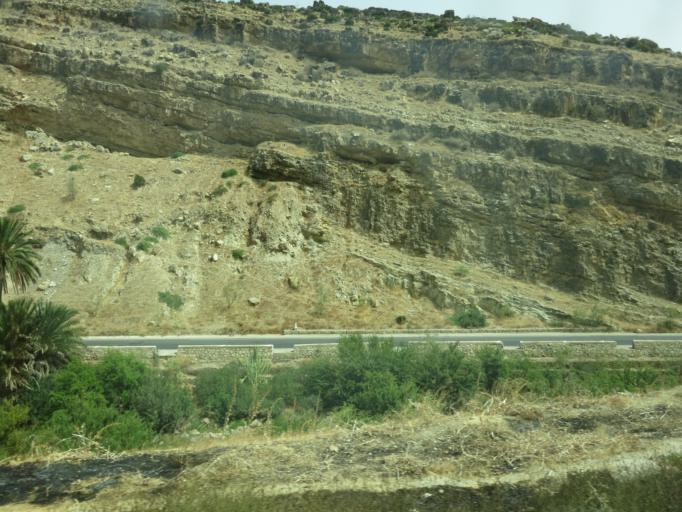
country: MA
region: Gharb-Chrarda-Beni Hssen
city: Sidi Qacem
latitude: 34.1830
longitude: -5.7061
